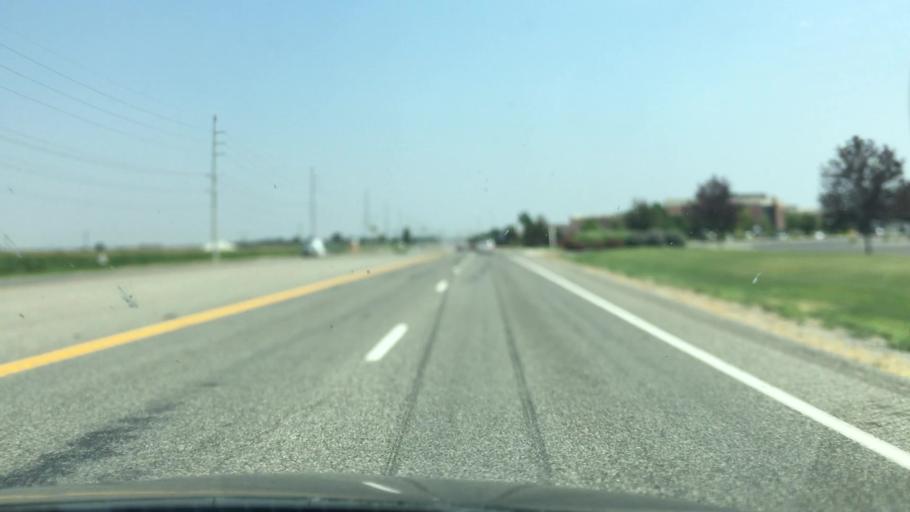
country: US
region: Idaho
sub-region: Twin Falls County
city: Twin Falls
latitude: 42.5916
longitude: -114.5035
